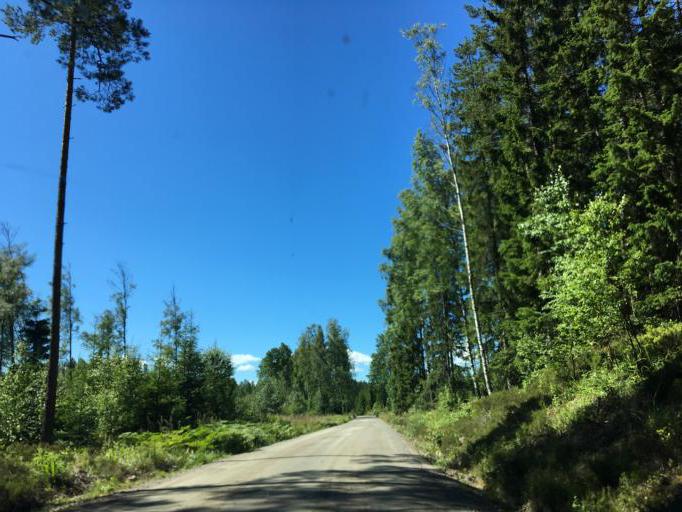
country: SE
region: Vaestra Goetaland
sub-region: Karlsborgs Kommun
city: Karlsborg
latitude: 58.7540
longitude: 14.5858
